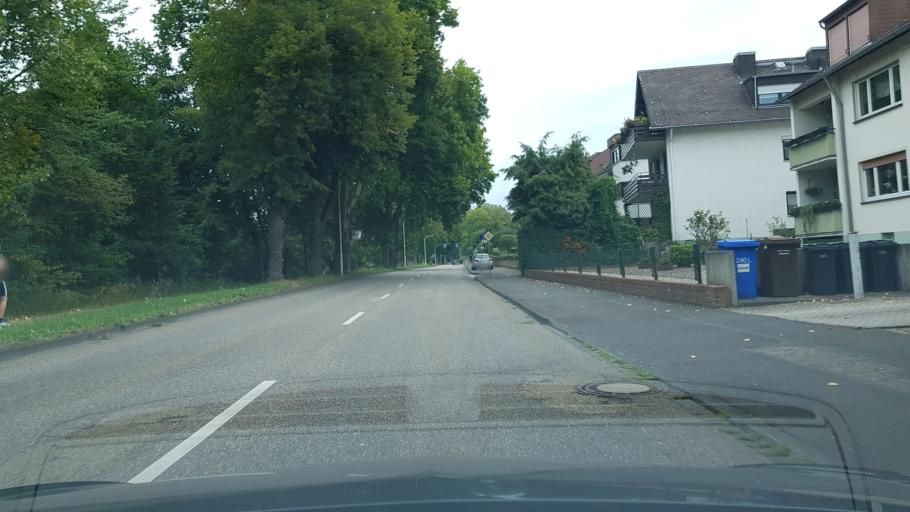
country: DE
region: Rheinland-Pfalz
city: Koblenz
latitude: 50.3490
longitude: 7.5548
